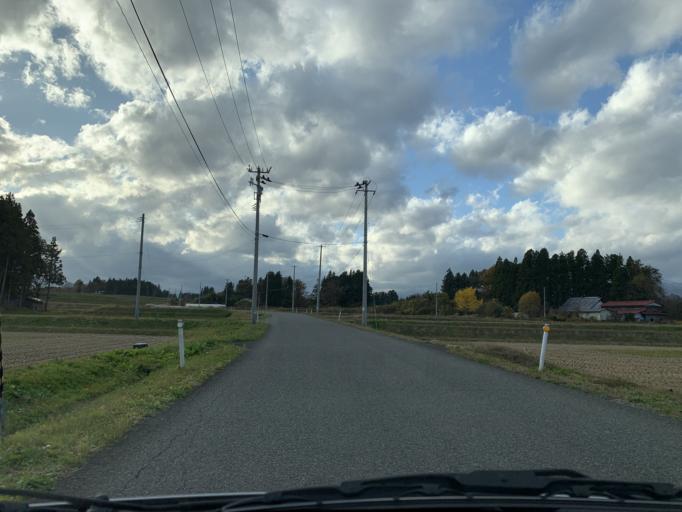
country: JP
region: Iwate
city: Mizusawa
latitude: 39.1095
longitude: 141.0296
